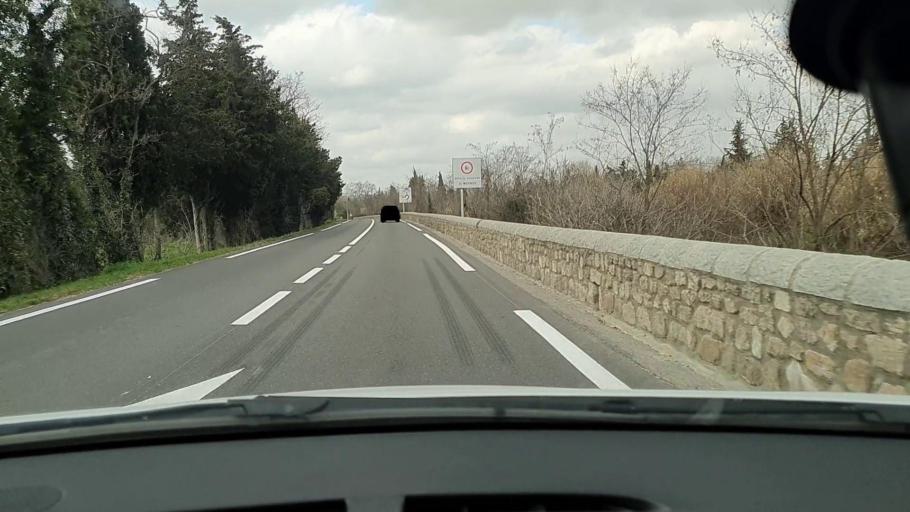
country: FR
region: Languedoc-Roussillon
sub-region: Departement du Gard
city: Meynes
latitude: 43.8778
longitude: 4.5780
